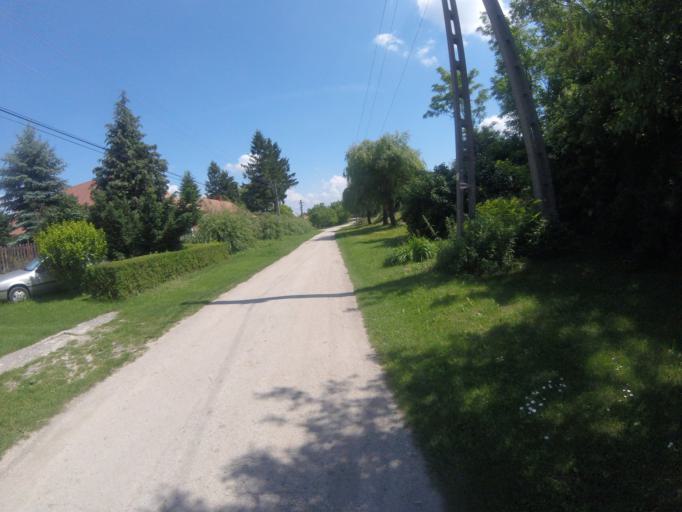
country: HU
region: Veszprem
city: Cseteny
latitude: 47.2573
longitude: 18.0249
